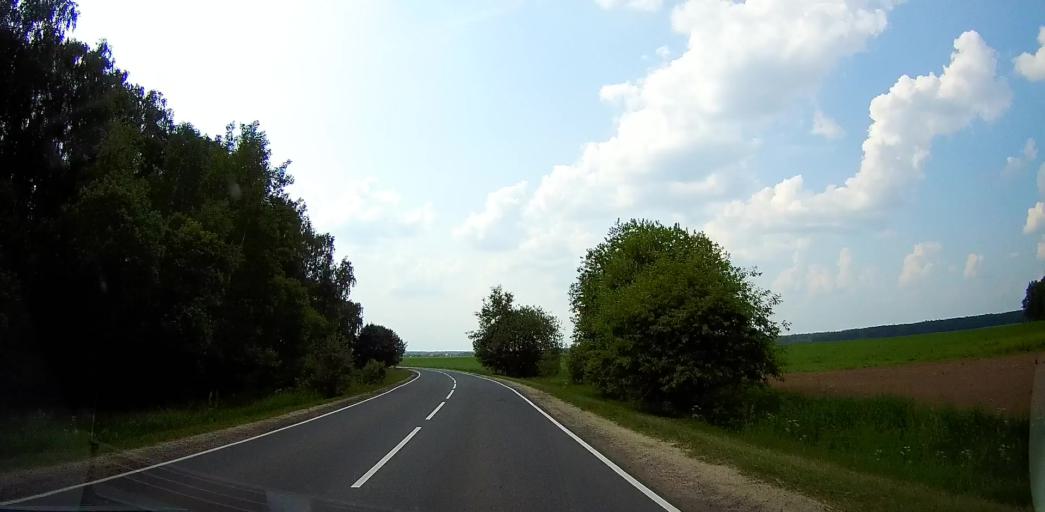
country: RU
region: Moskovskaya
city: Zhilevo
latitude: 55.0554
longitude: 38.0312
